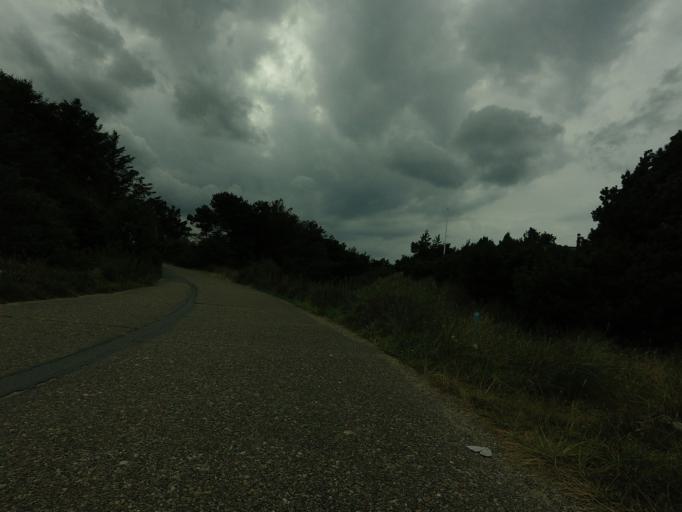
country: DK
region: North Denmark
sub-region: Jammerbugt Kommune
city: Pandrup
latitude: 57.3111
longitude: 9.6555
